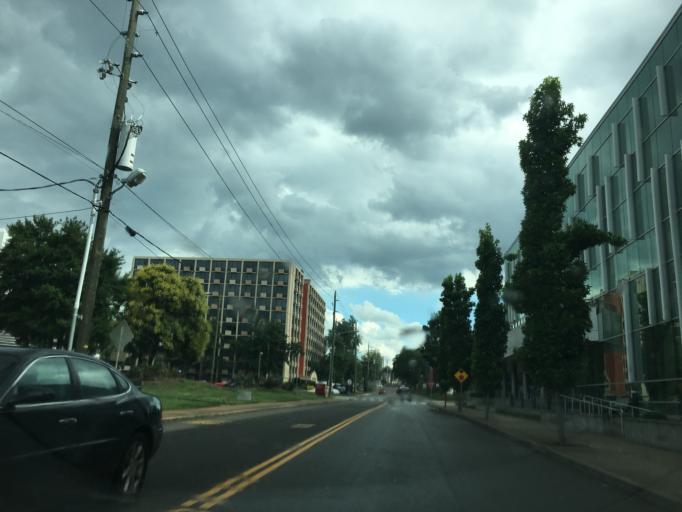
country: US
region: Tennessee
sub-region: Davidson County
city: Nashville
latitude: 36.1666
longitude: -86.8091
